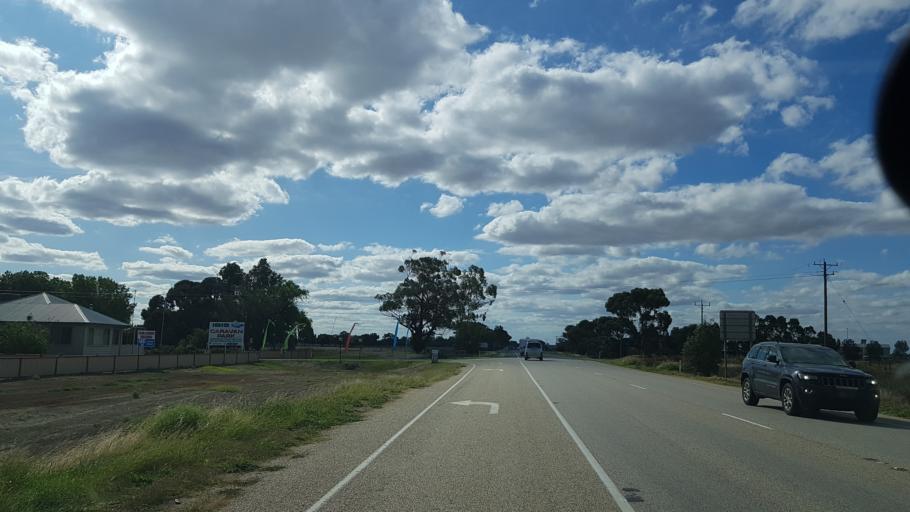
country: AU
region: Victoria
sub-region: Swan Hill
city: Swan Hill
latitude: -35.7608
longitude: 143.9299
